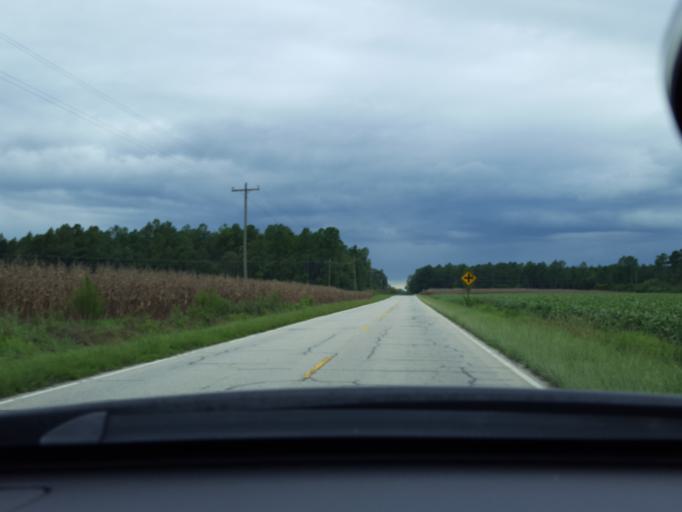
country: US
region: North Carolina
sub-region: Duplin County
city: Rose Hill
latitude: 34.8117
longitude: -78.1898
